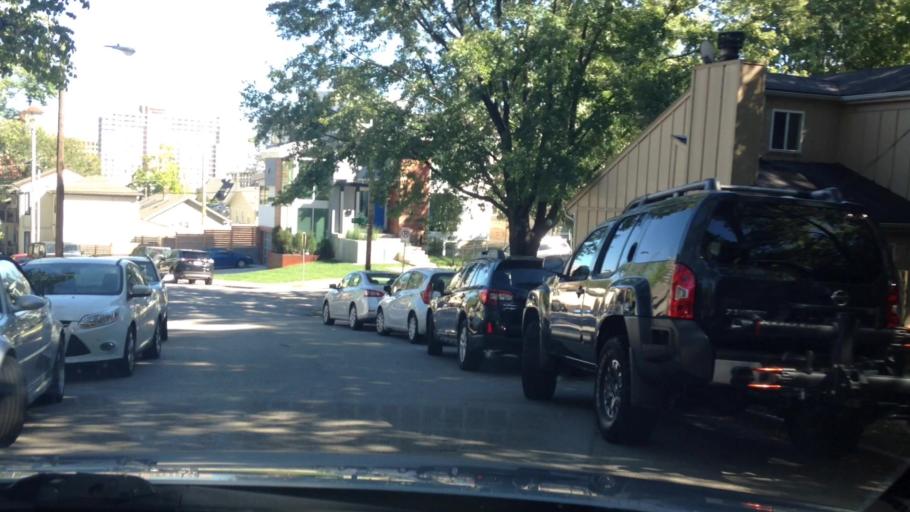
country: US
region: Kansas
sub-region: Johnson County
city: Westwood
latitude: 39.0441
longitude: -94.6021
